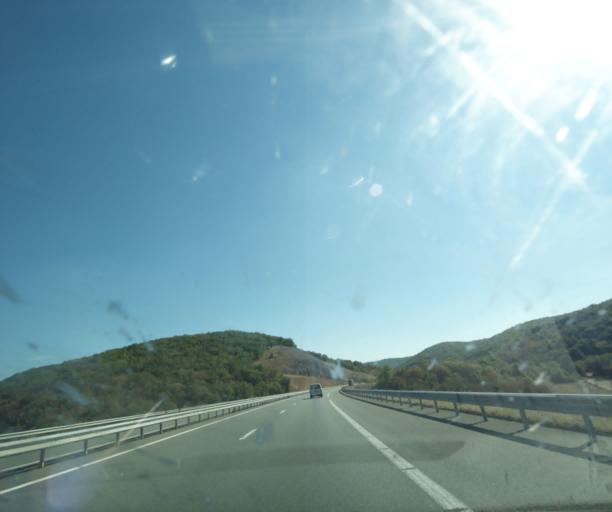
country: FR
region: Midi-Pyrenees
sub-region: Departement du Lot
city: Souillac
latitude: 44.8373
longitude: 1.4948
